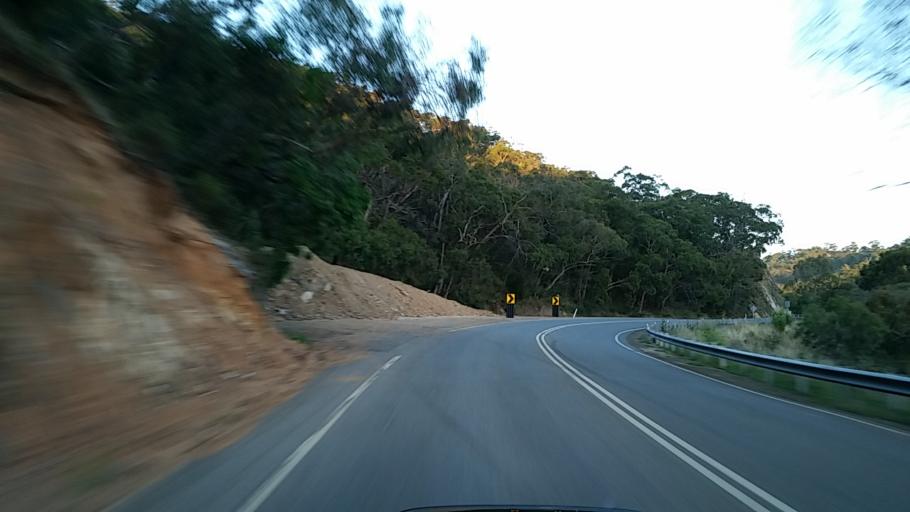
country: AU
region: South Australia
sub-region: Campbelltown
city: Athelstone
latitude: -34.8643
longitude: 138.7766
